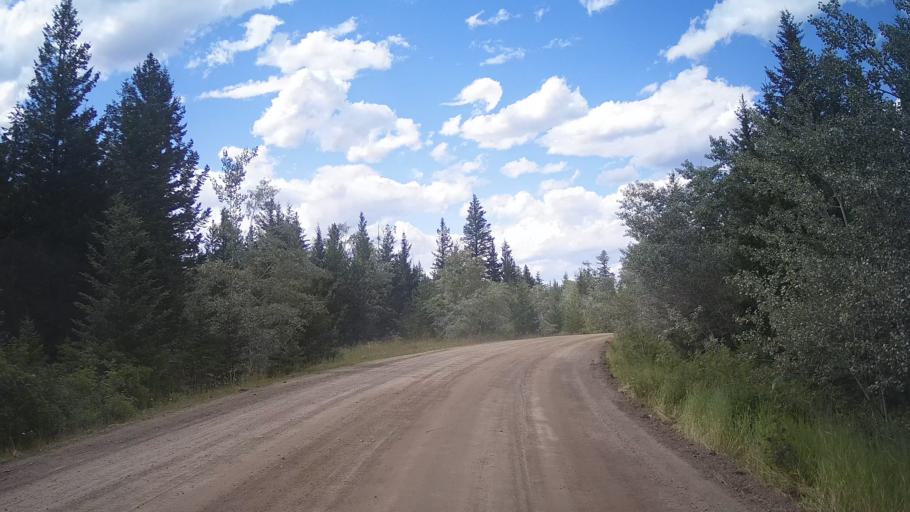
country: CA
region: British Columbia
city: Lillooet
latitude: 51.3359
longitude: -121.9064
